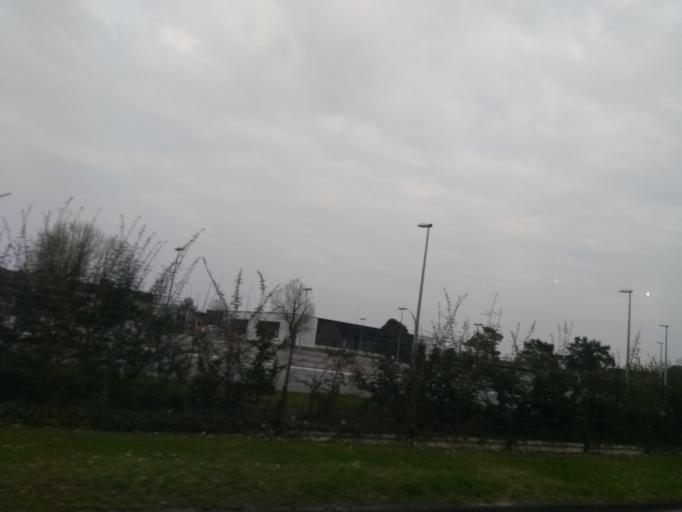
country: FR
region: Picardie
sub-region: Departement de l'Oise
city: Jaux
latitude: 49.3898
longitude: 2.7826
